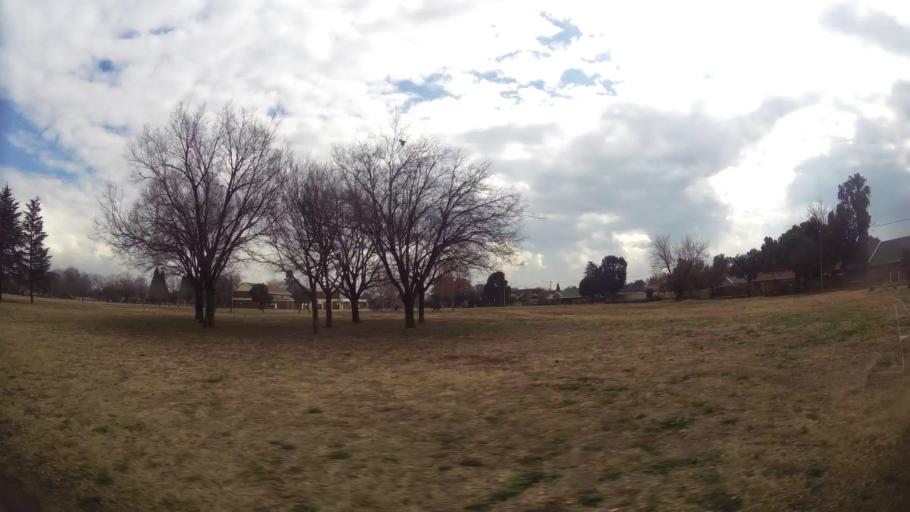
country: ZA
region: Gauteng
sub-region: Sedibeng District Municipality
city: Vereeniging
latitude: -26.6418
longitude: 27.9786
